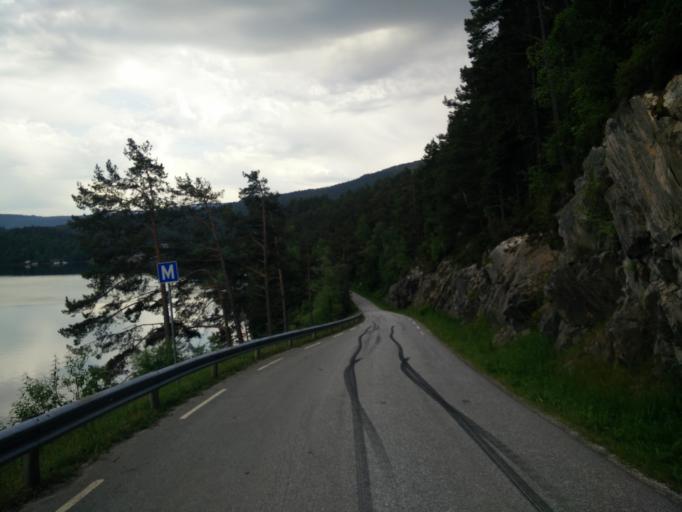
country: NO
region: More og Romsdal
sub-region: Kristiansund
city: Rensvik
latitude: 63.0290
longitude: 7.9543
